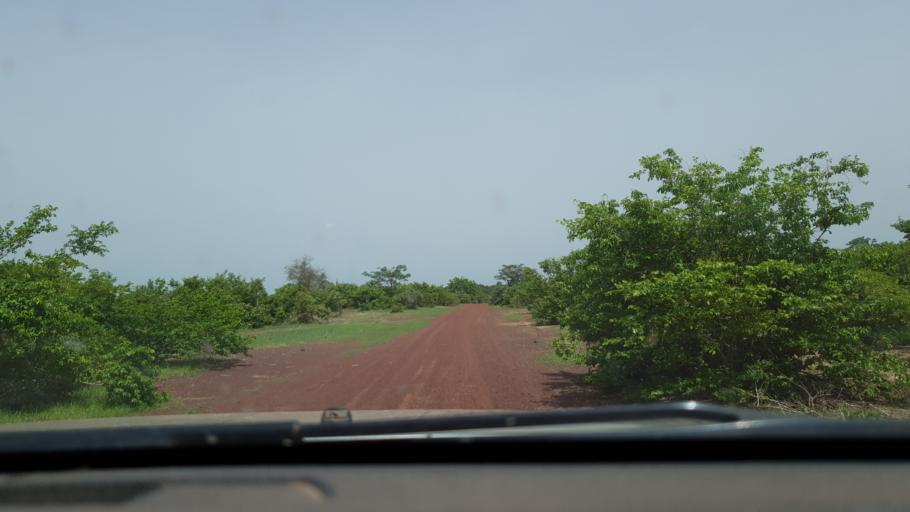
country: ML
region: Koulikoro
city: Koulikoro
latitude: 12.6664
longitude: -7.2338
